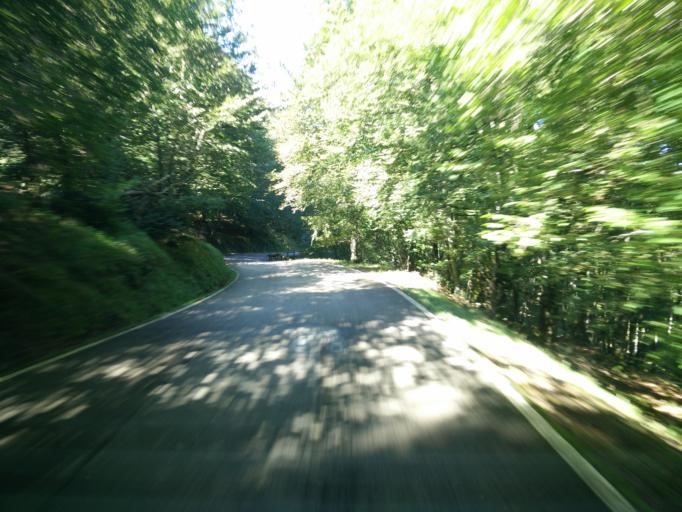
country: ES
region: Cantabria
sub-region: Provincia de Cantabria
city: Ruente
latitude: 43.1087
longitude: -4.2822
